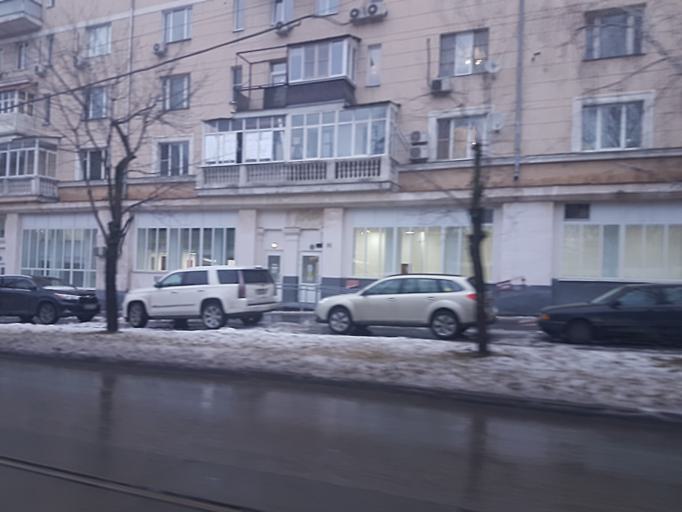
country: RU
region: Moskovskaya
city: Kozhukhovo
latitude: 55.6781
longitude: 37.6548
